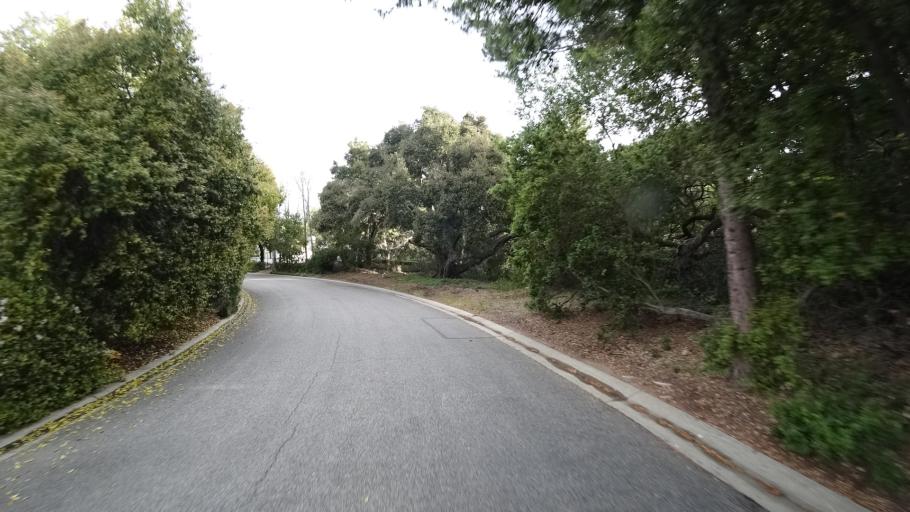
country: US
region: California
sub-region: Ventura County
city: Thousand Oaks
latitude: 34.1811
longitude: -118.8205
